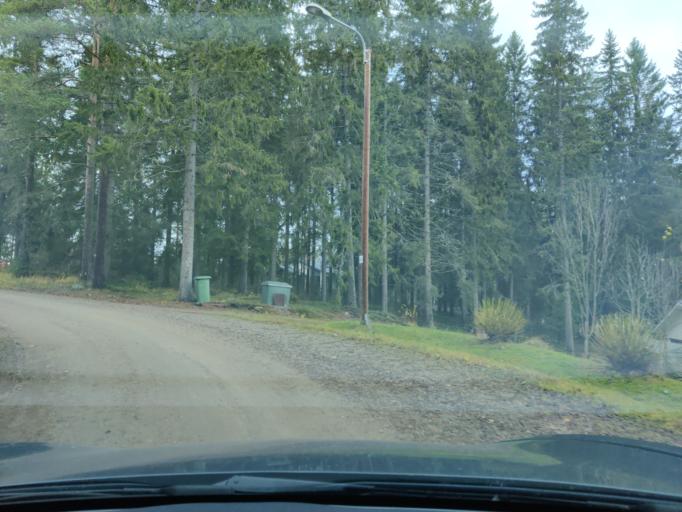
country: FI
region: Northern Savo
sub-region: Ylae-Savo
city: Kiuruvesi
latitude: 63.6450
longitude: 26.6437
